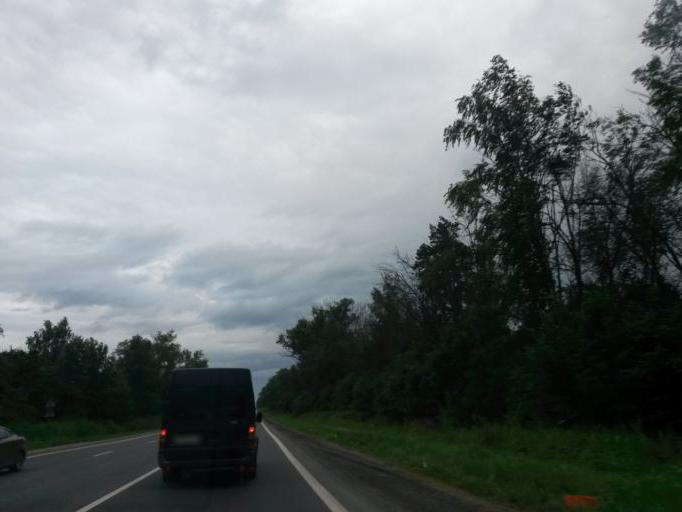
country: RU
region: Moskovskaya
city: Belyye Stolby
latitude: 55.3019
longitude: 37.8158
